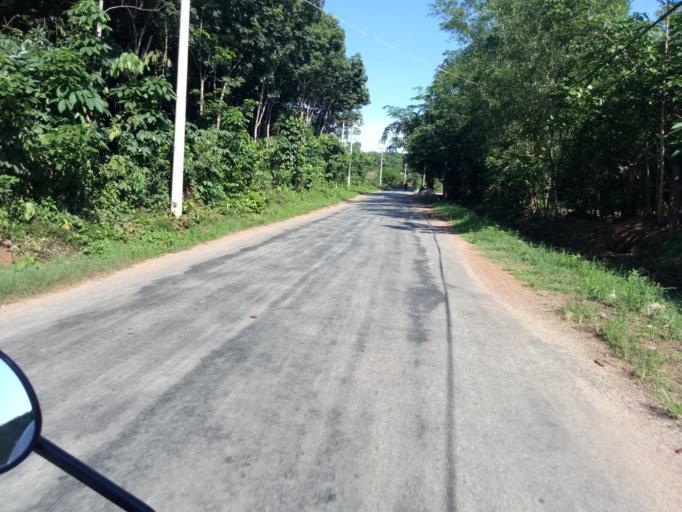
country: MM
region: Mon
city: Mawlamyine
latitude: 16.3777
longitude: 97.5525
